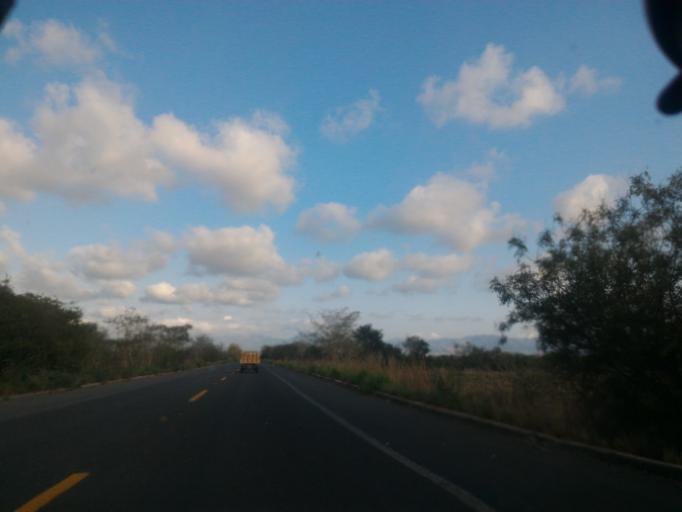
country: MX
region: Michoacan
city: Coahuayana Viejo
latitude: 18.7798
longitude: -103.7623
